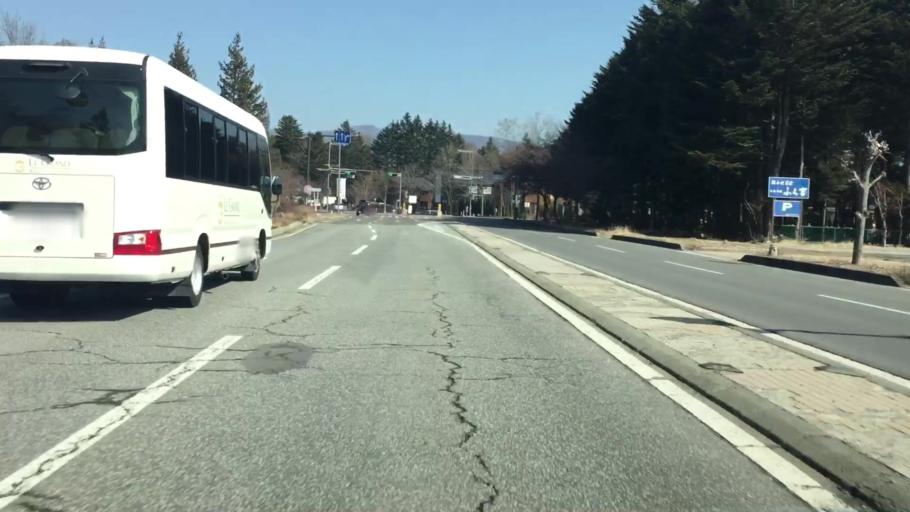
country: JP
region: Nagano
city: Saku
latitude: 36.3320
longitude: 138.6312
